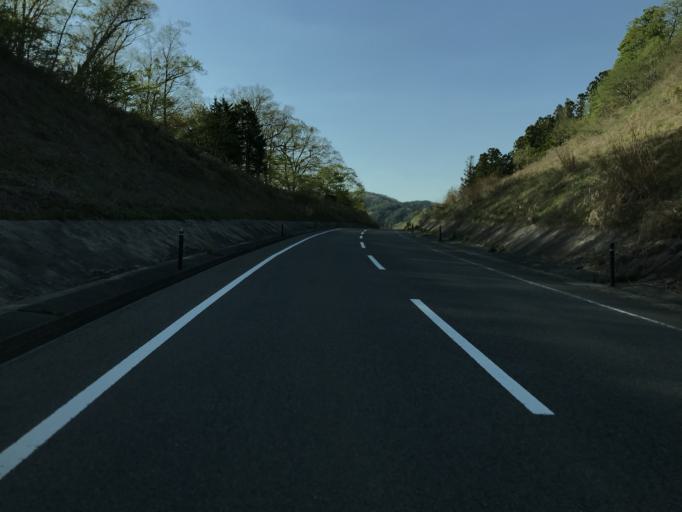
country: JP
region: Fukushima
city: Funehikimachi-funehiki
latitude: 37.5181
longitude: 140.7515
